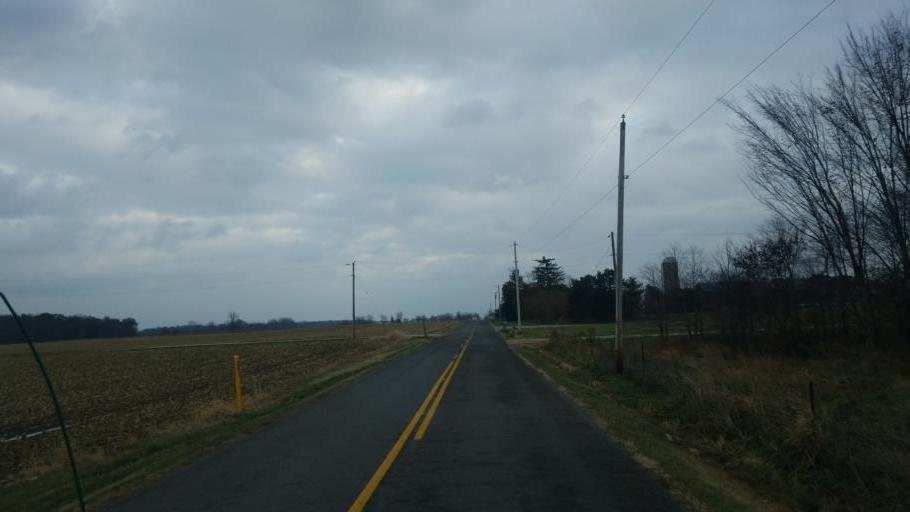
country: US
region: Ohio
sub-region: Mercer County
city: Coldwater
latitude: 40.5090
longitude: -84.7239
